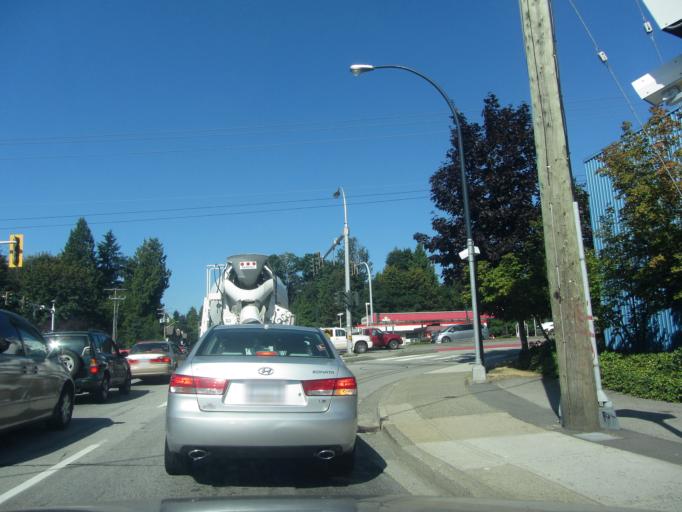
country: CA
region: British Columbia
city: Delta
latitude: 49.1772
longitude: -122.8450
